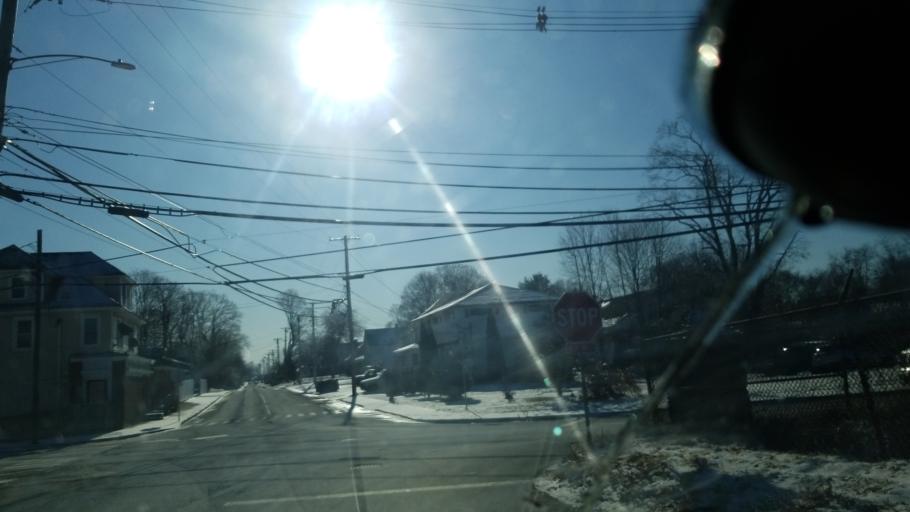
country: US
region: Connecticut
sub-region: Windham County
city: Danielson
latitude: 41.8165
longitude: -71.8836
